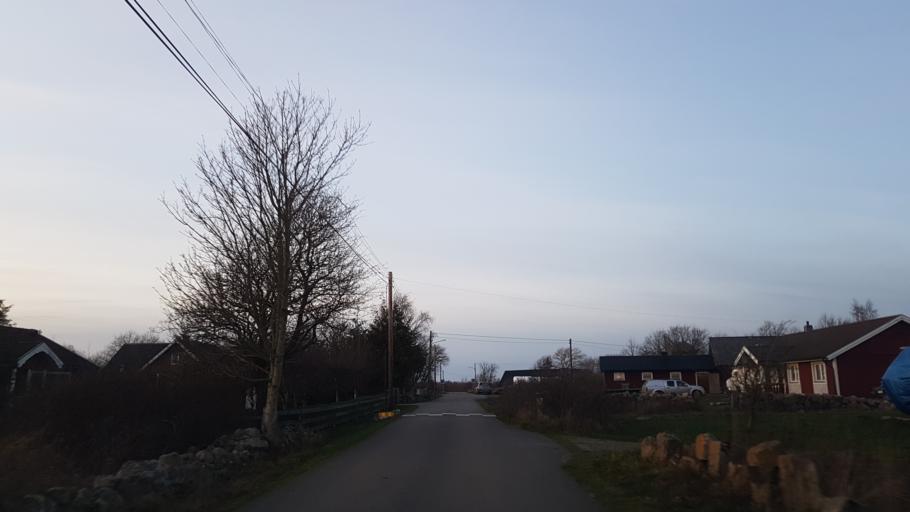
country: SE
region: Blekinge
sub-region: Karlskrona Kommun
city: Jaemjoe
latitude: 56.0880
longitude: 15.8369
